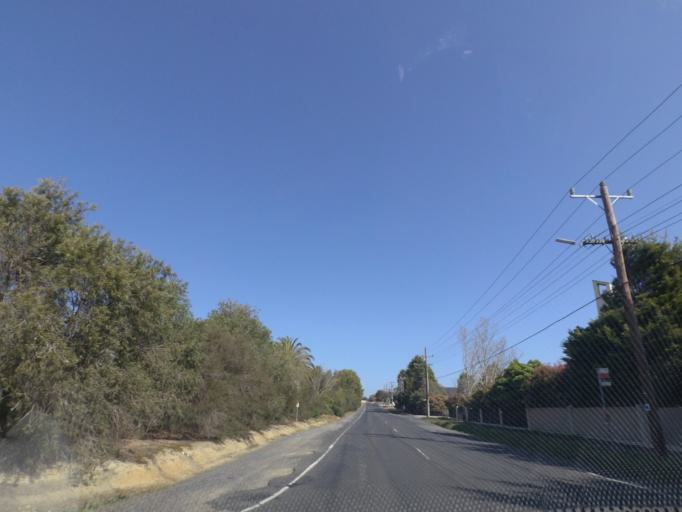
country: AU
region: Victoria
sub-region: Manningham
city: Doncaster East
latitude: -37.7717
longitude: 145.1555
